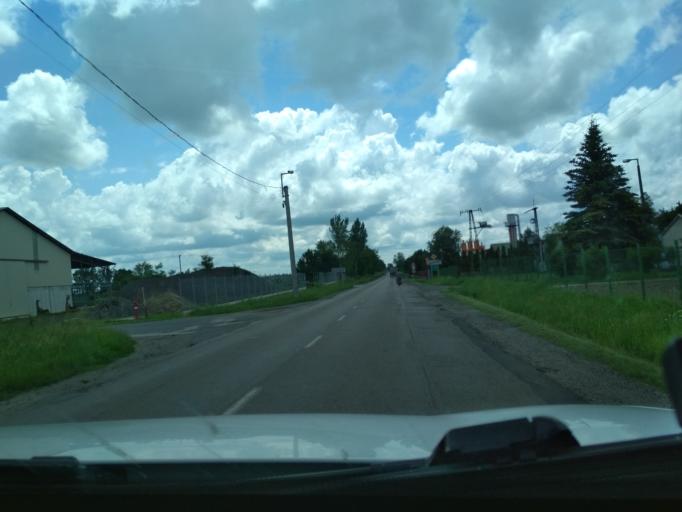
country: HU
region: Jasz-Nagykun-Szolnok
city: Tiszafured
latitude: 47.6019
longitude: 20.7641
